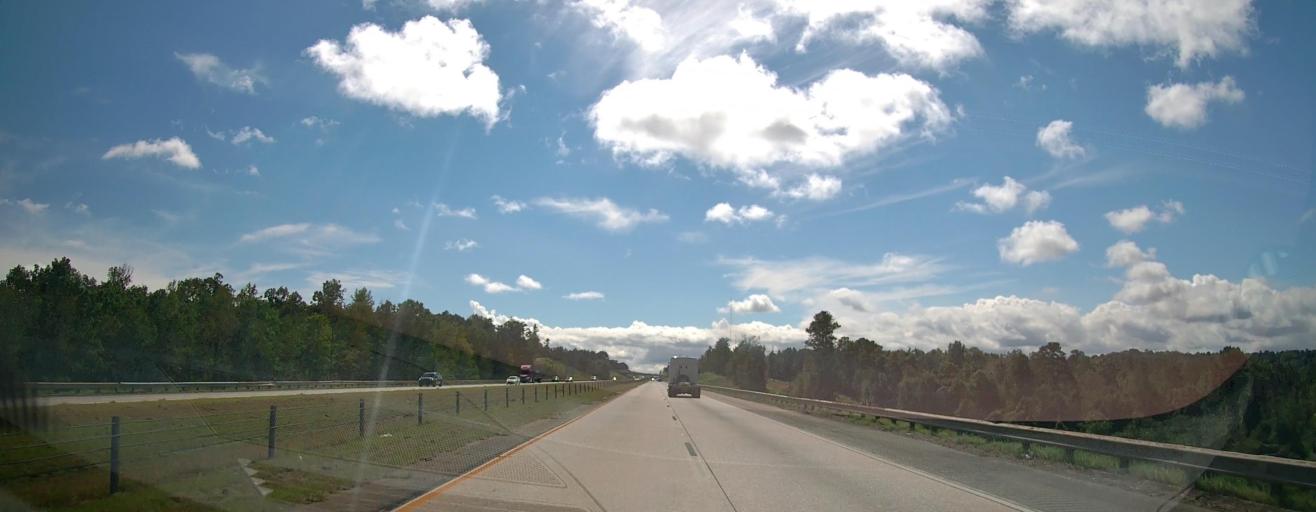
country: US
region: Georgia
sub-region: Bibb County
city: Macon
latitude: 32.7834
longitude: -83.5592
